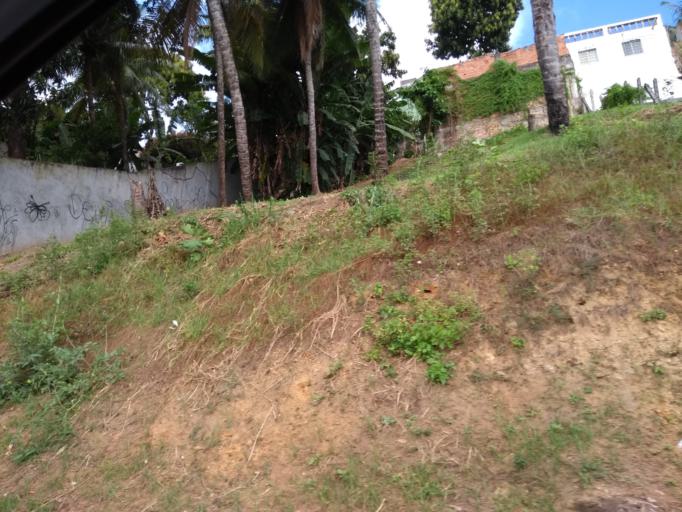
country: BR
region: Bahia
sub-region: Salvador
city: Salvador
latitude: -12.9833
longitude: -38.5204
